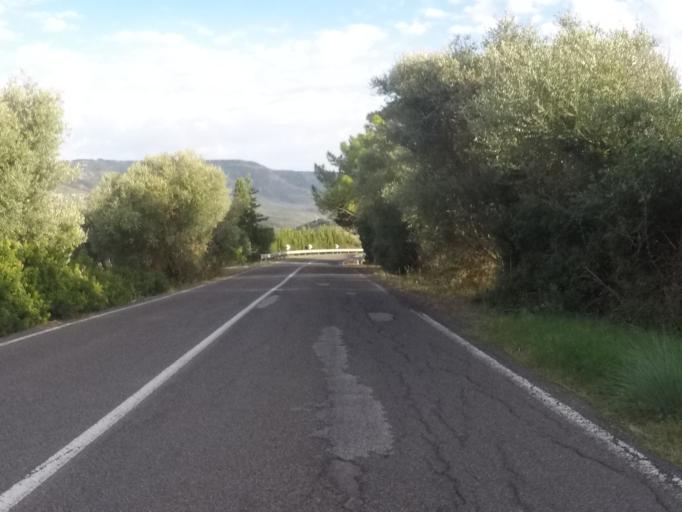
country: IT
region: Sardinia
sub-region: Provincia di Sassari
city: Alghero
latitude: 40.5108
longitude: 8.3560
